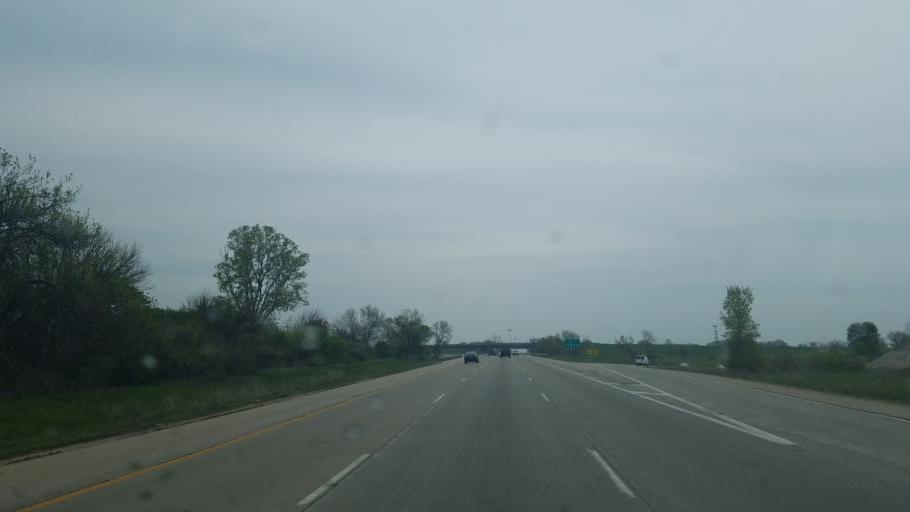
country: US
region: Wisconsin
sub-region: Dane County
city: Monona
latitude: 43.0994
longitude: -89.2836
